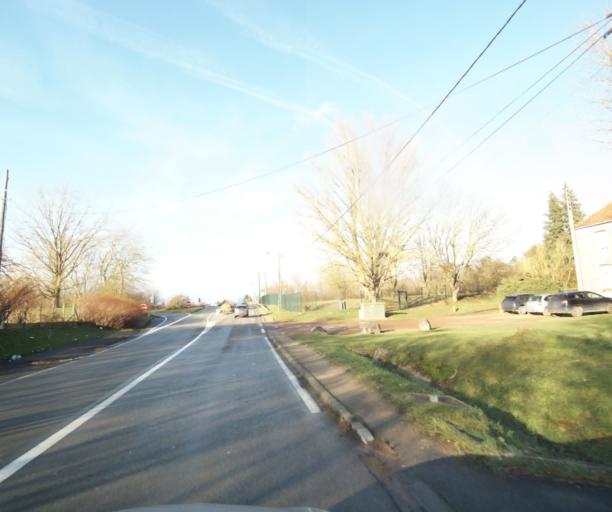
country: FR
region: Nord-Pas-de-Calais
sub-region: Departement du Nord
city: Marly
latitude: 50.3349
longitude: 3.5557
